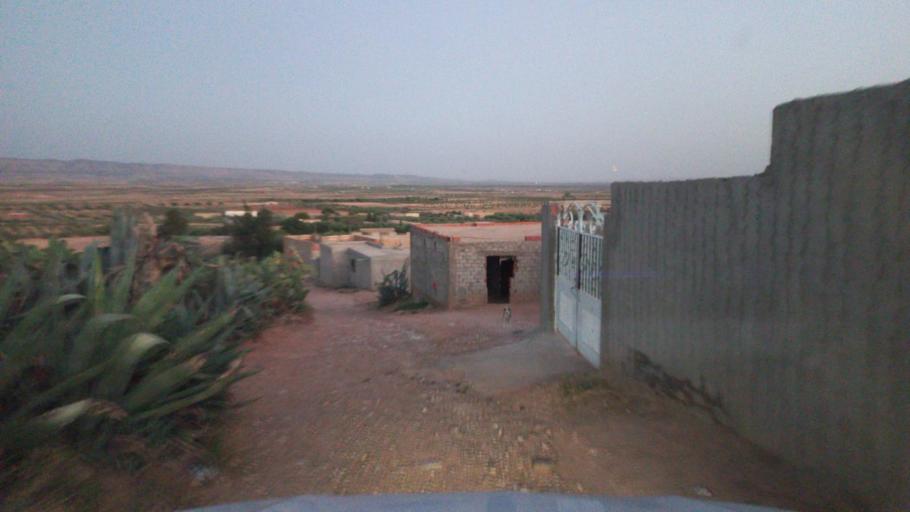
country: TN
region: Al Qasrayn
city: Sbiba
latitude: 35.3790
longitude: 9.0141
